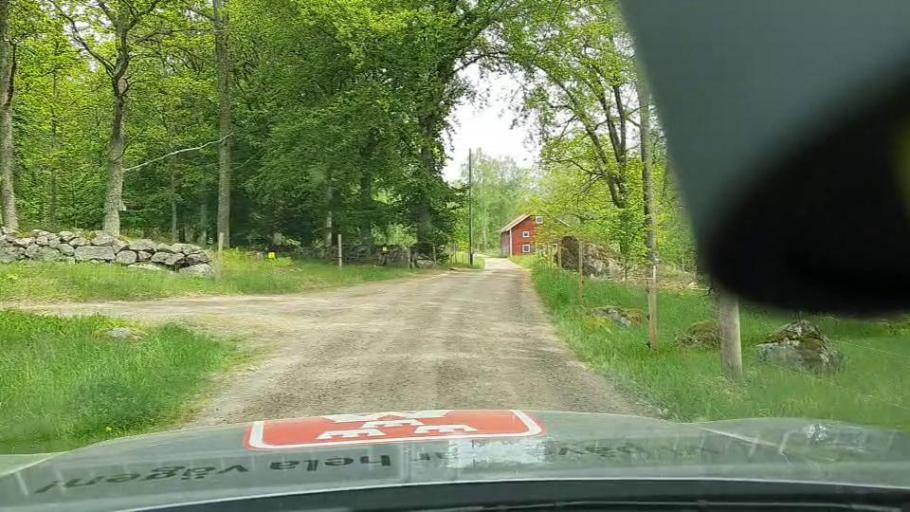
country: SE
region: Soedermanland
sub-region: Flens Kommun
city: Flen
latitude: 59.0417
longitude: 16.5718
